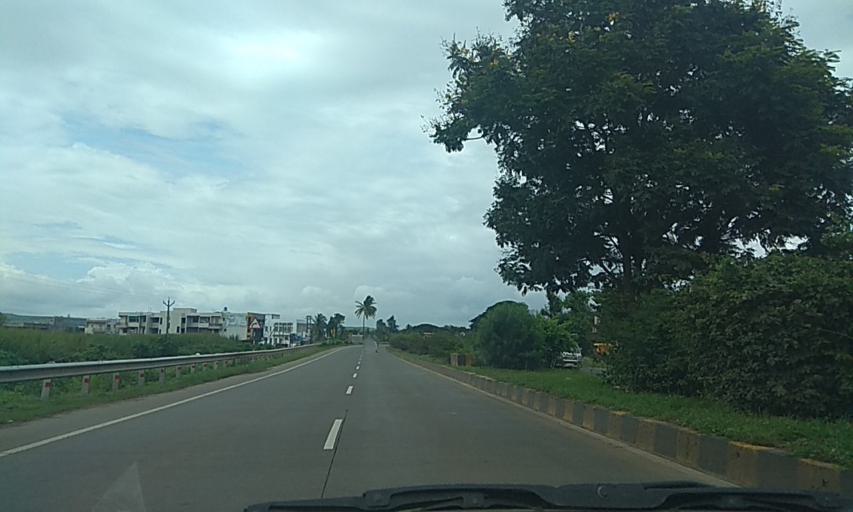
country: IN
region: Maharashtra
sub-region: Kolhapur
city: Kagal
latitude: 16.5728
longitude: 74.3133
